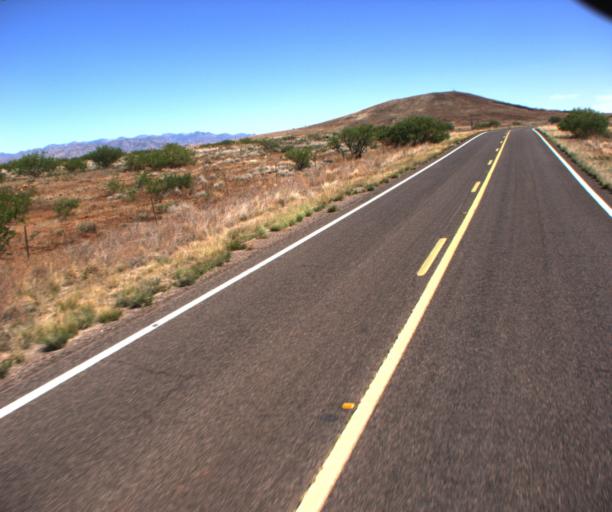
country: US
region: Arizona
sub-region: Cochise County
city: Douglas
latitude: 31.5447
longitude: -109.2834
